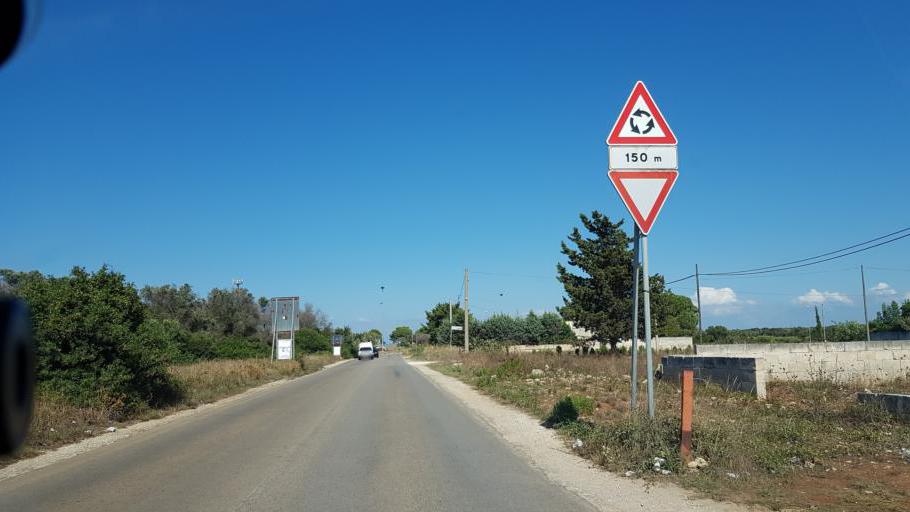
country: IT
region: Apulia
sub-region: Provincia di Lecce
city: Porto Cesareo
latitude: 40.2234
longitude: 17.9372
